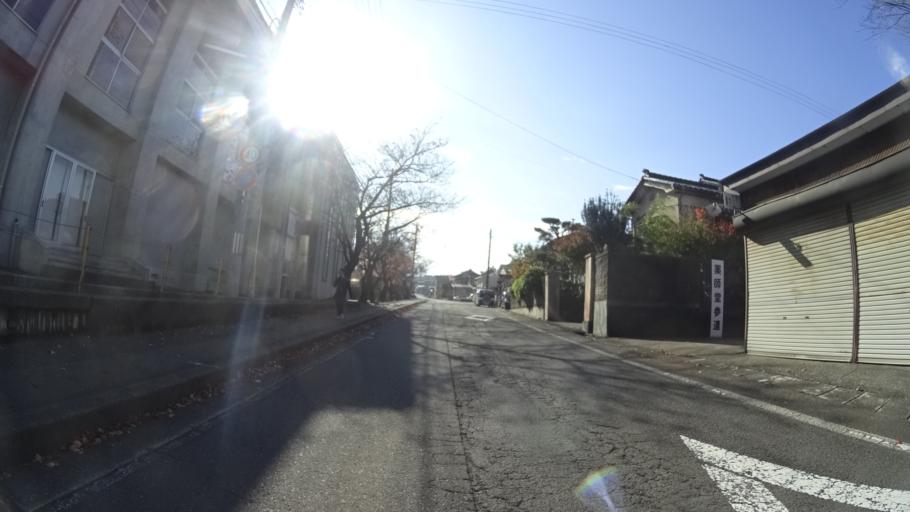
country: JP
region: Niigata
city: Itoigawa
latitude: 37.0342
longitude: 137.8581
